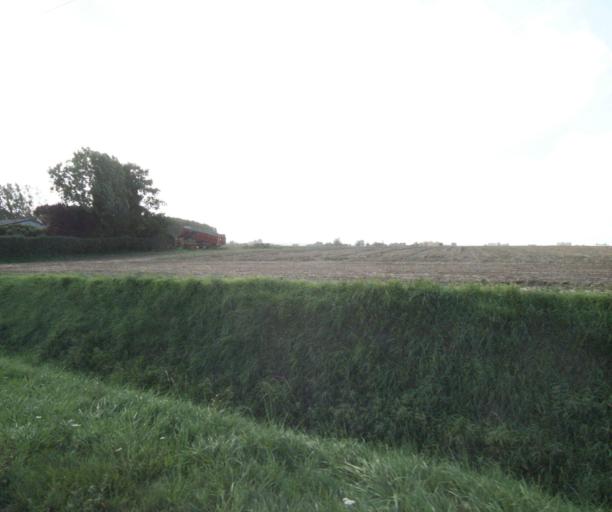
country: FR
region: Nord-Pas-de-Calais
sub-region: Departement du Nord
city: Herlies
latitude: 50.5667
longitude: 2.8580
